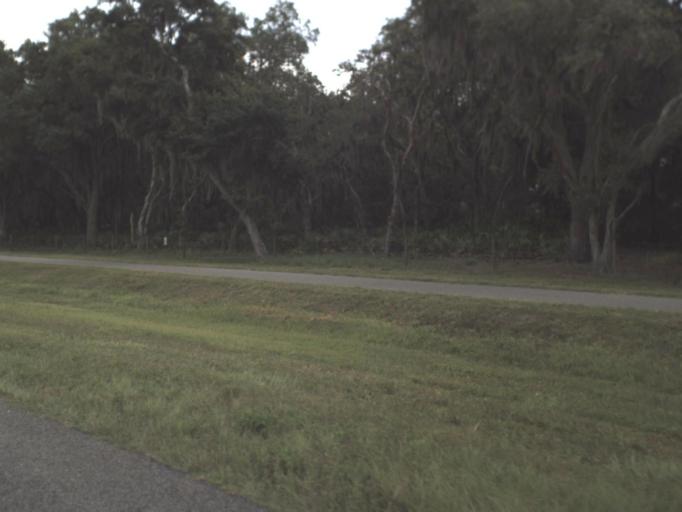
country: US
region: Florida
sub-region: Pasco County
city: Wesley Chapel
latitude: 28.1977
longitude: -82.3066
